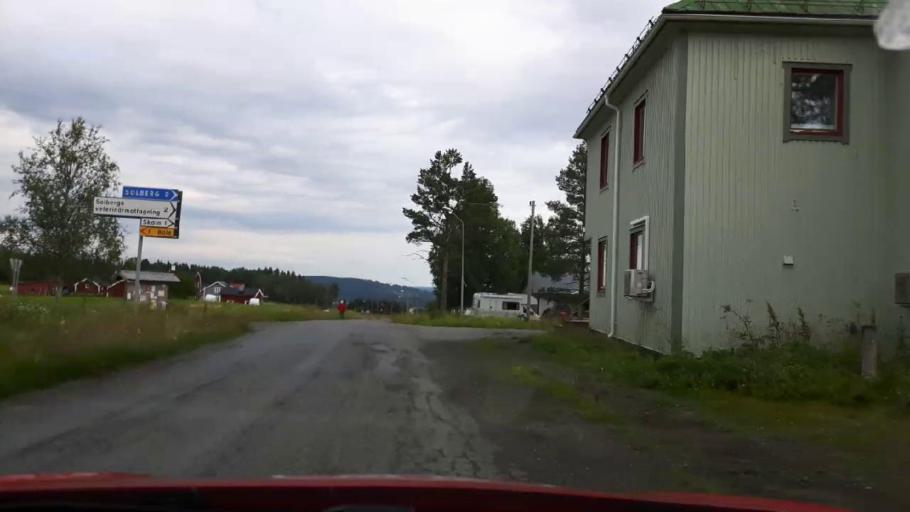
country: SE
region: Jaemtland
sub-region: Stroemsunds Kommun
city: Stroemsund
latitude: 63.5229
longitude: 15.3547
